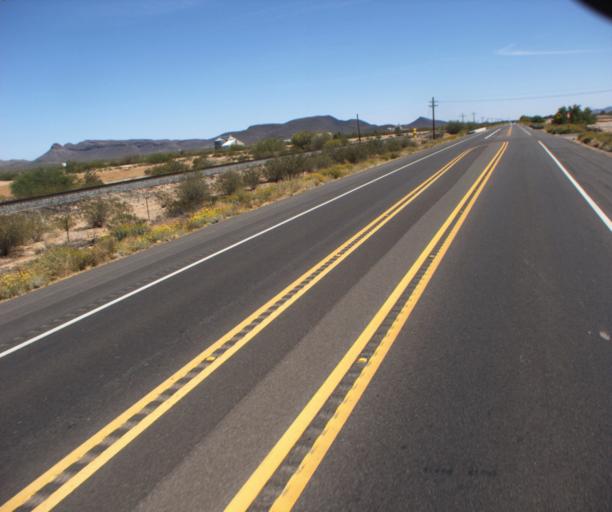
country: US
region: Arizona
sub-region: Pinal County
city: Sacaton
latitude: 33.1477
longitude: -111.7664
